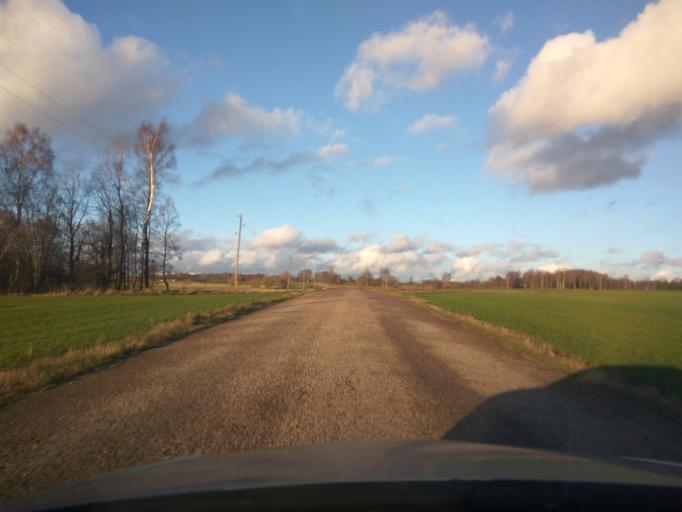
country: LV
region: Aizpute
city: Aizpute
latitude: 56.7642
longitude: 21.7824
